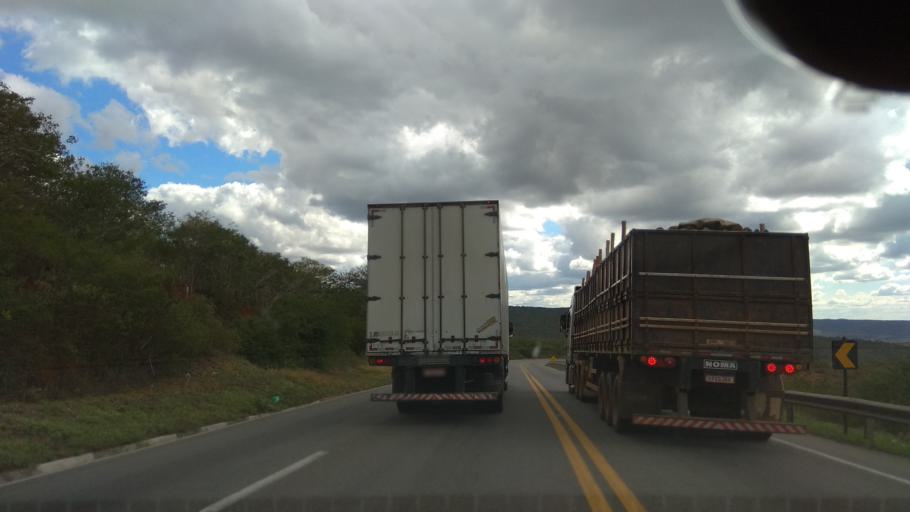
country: BR
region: Bahia
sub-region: Santa Ines
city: Santa Ines
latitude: -13.0442
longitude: -39.9642
